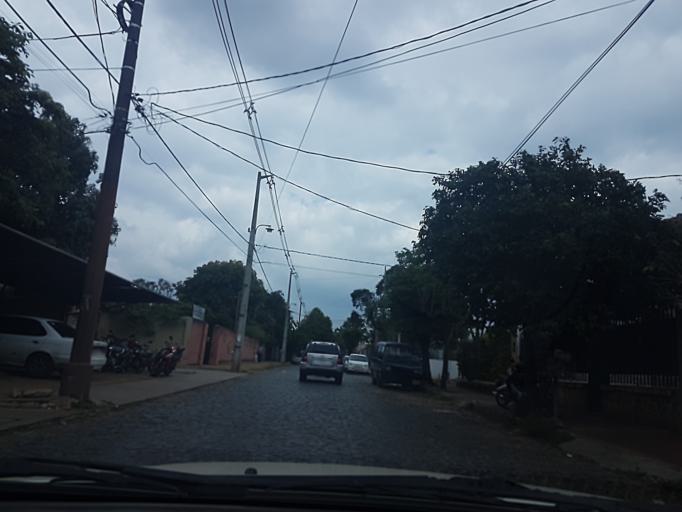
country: PY
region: Asuncion
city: Asuncion
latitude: -25.3082
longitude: -57.6001
